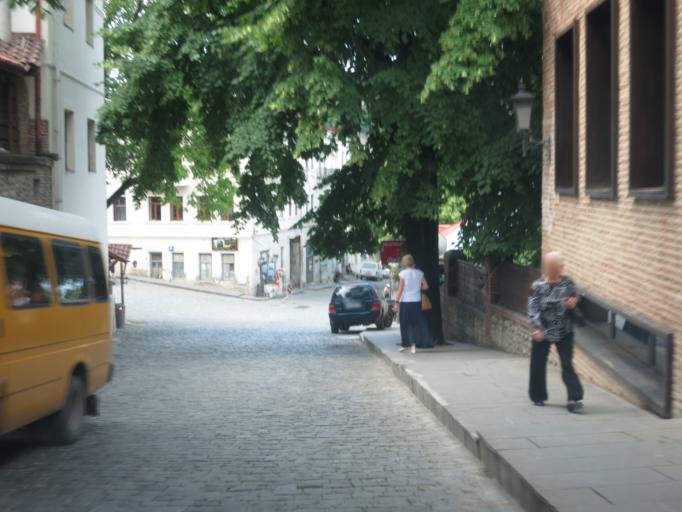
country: GE
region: Kakheti
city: Sighnaghi
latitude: 41.6197
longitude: 45.9224
